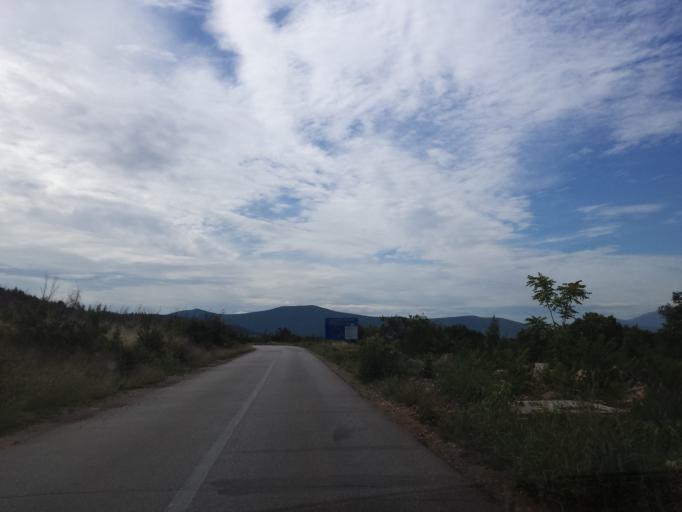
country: BA
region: Federation of Bosnia and Herzegovina
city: Citluk
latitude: 43.1847
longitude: 17.6474
